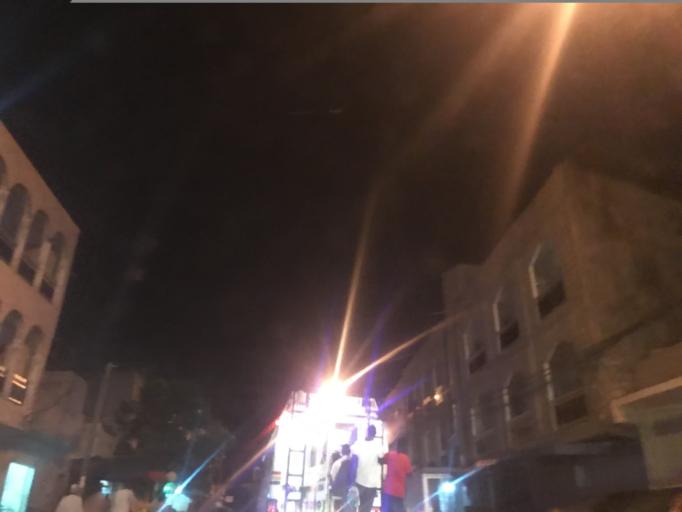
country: SN
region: Dakar
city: Grand Dakar
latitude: 14.7512
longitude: -17.4464
